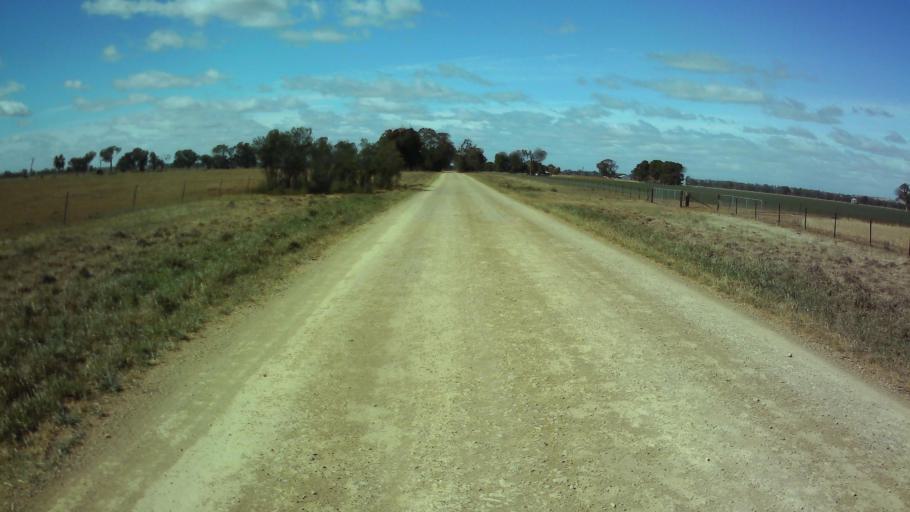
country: AU
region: New South Wales
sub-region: Weddin
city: Grenfell
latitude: -34.0240
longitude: 148.3184
